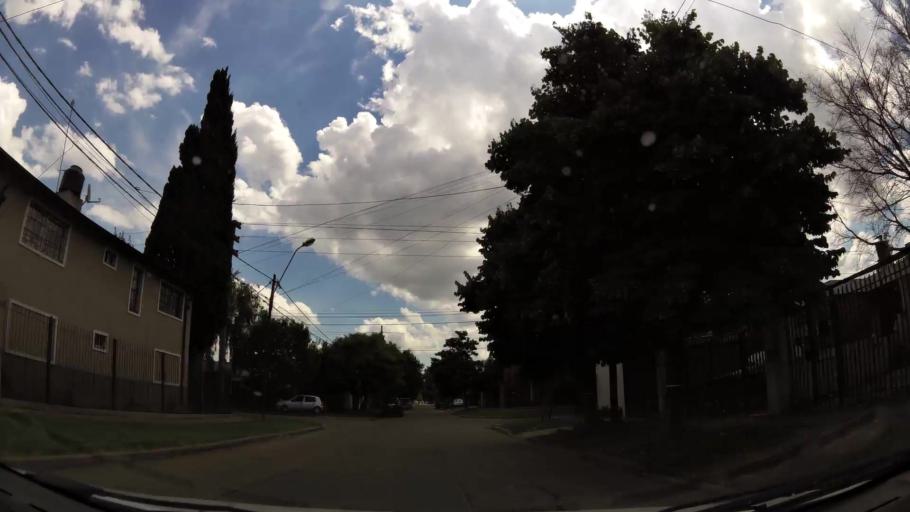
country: AR
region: Buenos Aires
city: Ituzaingo
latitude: -34.6485
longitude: -58.6696
